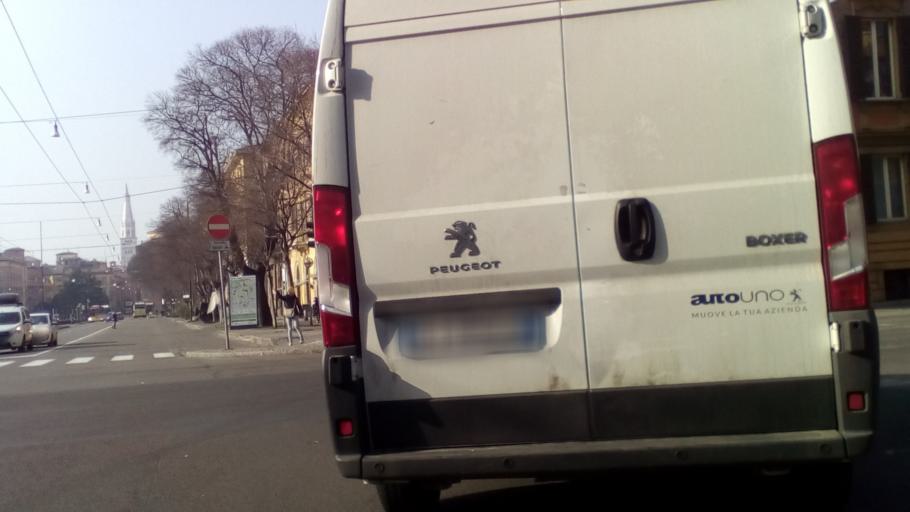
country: IT
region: Emilia-Romagna
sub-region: Provincia di Modena
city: Modena
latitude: 44.6433
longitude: 10.9338
